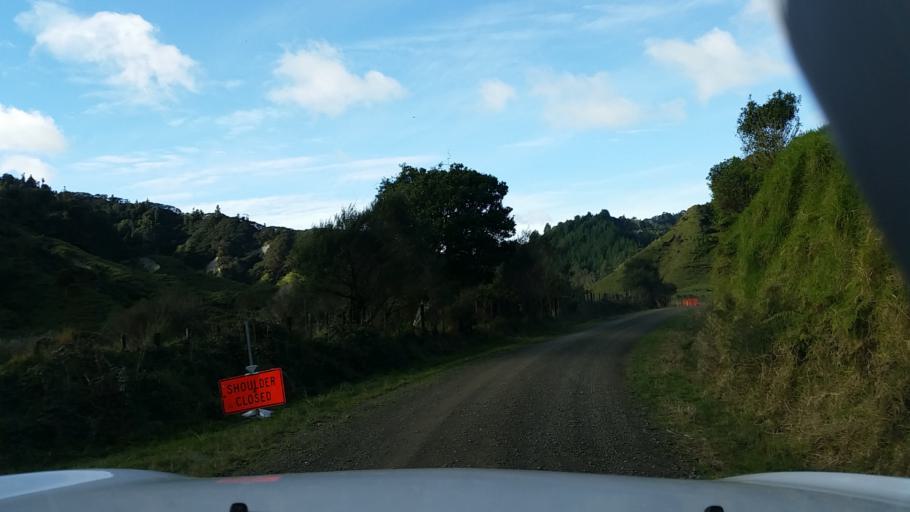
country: NZ
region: Taranaki
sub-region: New Plymouth District
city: Waitara
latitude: -38.9822
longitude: 174.4791
